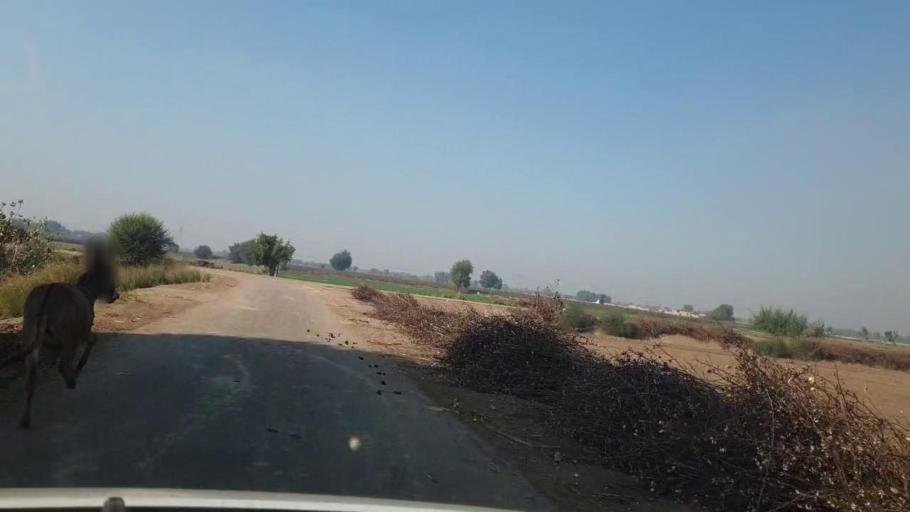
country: PK
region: Sindh
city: Bhan
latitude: 26.6116
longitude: 67.7610
